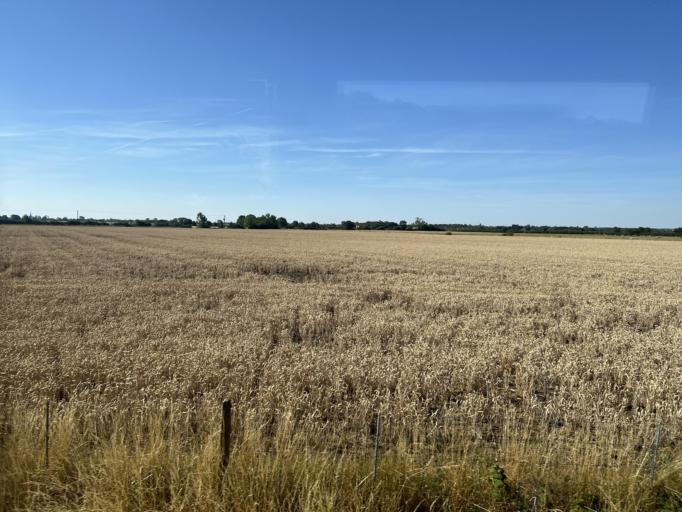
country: GB
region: England
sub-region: Lincolnshire
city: Heckington
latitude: 52.9818
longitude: -0.3176
